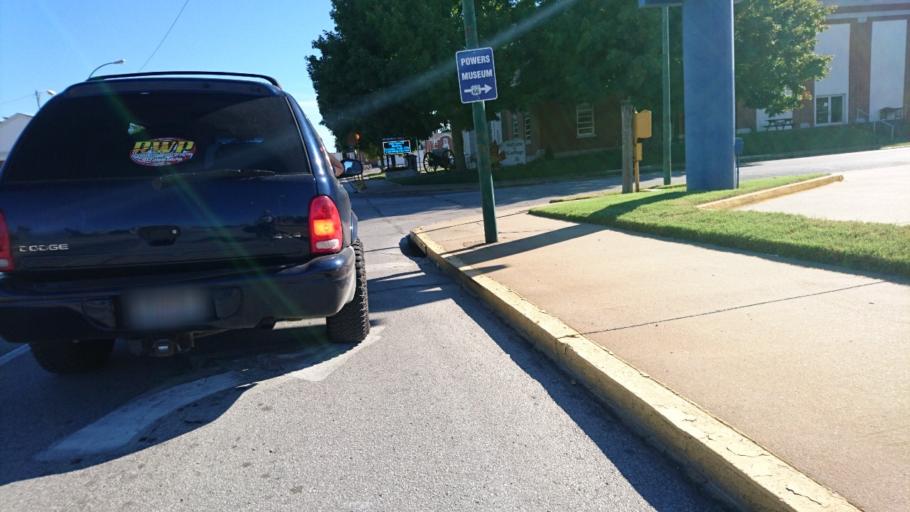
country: US
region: Missouri
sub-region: Jasper County
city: Carthage
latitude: 37.1766
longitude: -94.3141
